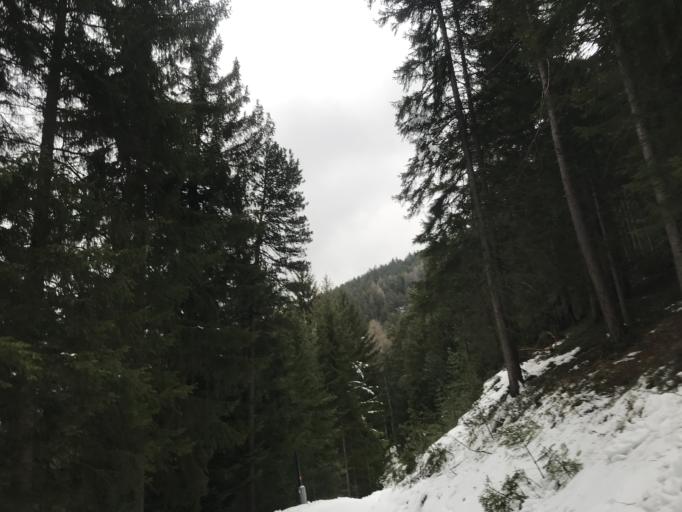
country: IT
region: Trentino-Alto Adige
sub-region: Bolzano
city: Funes - Villnoess
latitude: 46.6819
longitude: 11.6841
